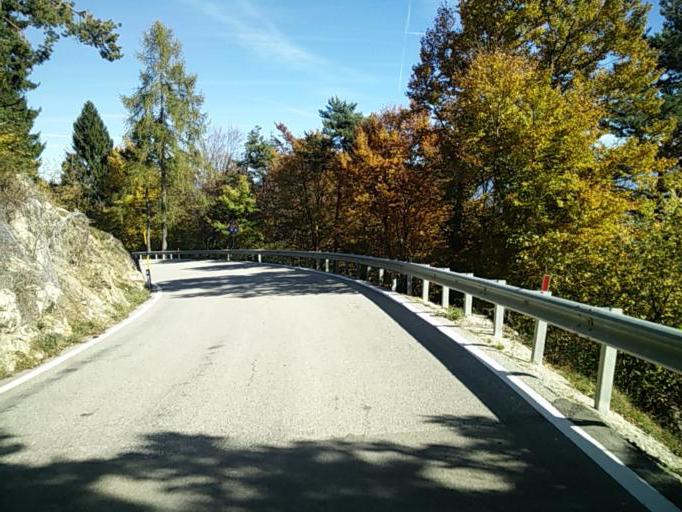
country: IT
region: Trentino-Alto Adige
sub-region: Provincia di Trento
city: Cadine
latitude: 46.0582
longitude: 11.0777
